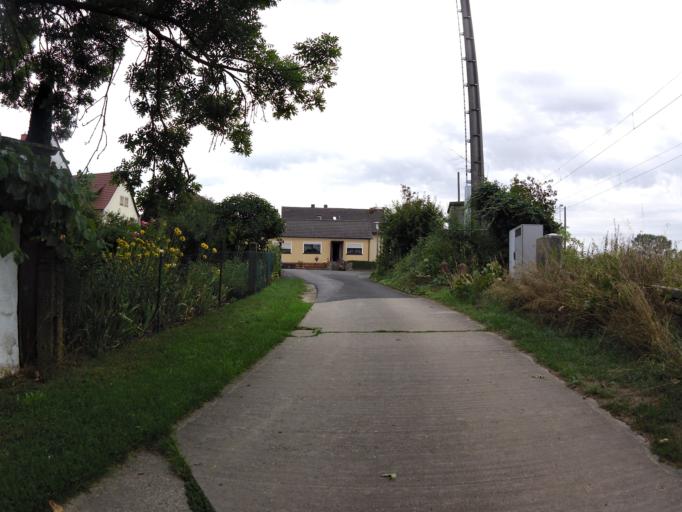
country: DE
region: Bavaria
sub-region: Regierungsbezirk Unterfranken
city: Donnersdorf
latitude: 50.0155
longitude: 10.4142
